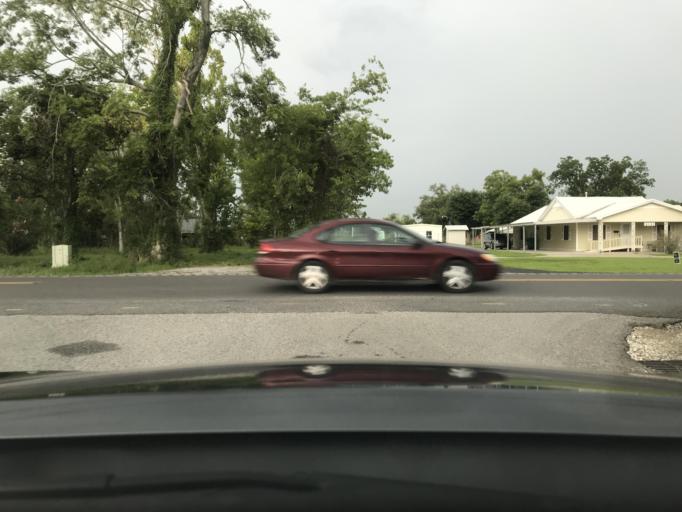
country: US
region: Louisiana
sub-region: Calcasieu Parish
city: Westlake
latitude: 30.2570
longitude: -93.2454
